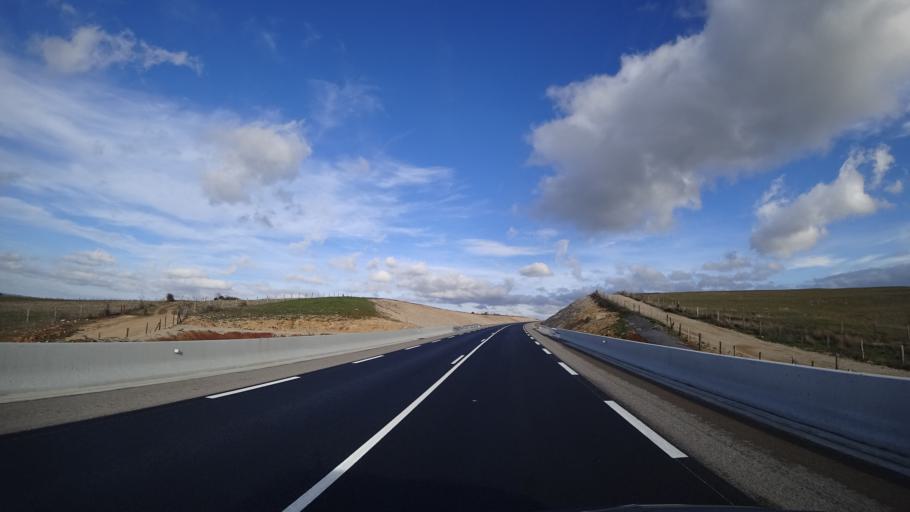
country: FR
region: Midi-Pyrenees
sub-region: Departement de l'Aveyron
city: Sebazac-Concoures
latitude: 44.4139
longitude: 2.6312
